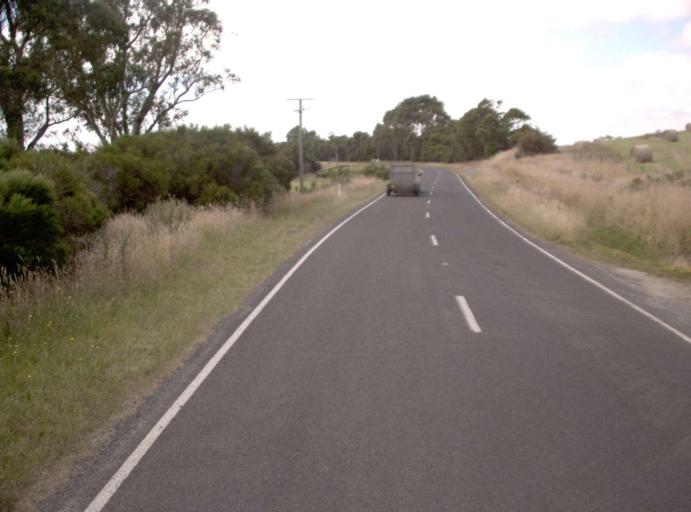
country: AU
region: Victoria
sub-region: Cardinia
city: Bunyip
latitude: -38.3369
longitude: 145.7311
